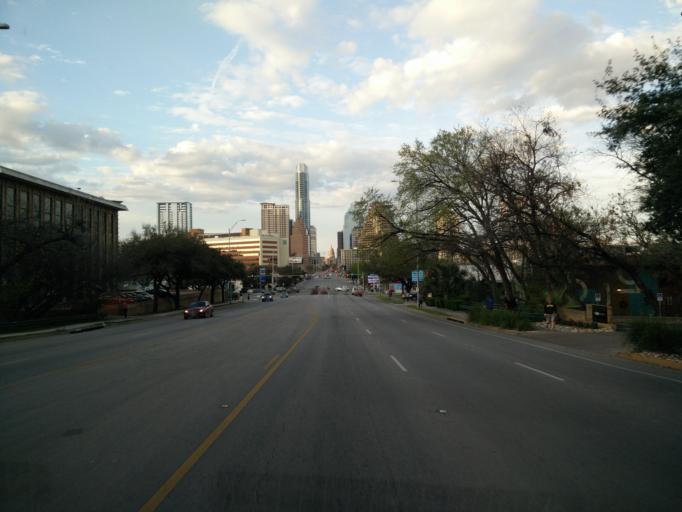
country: US
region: Texas
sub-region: Travis County
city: Austin
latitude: 30.2555
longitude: -97.7474
